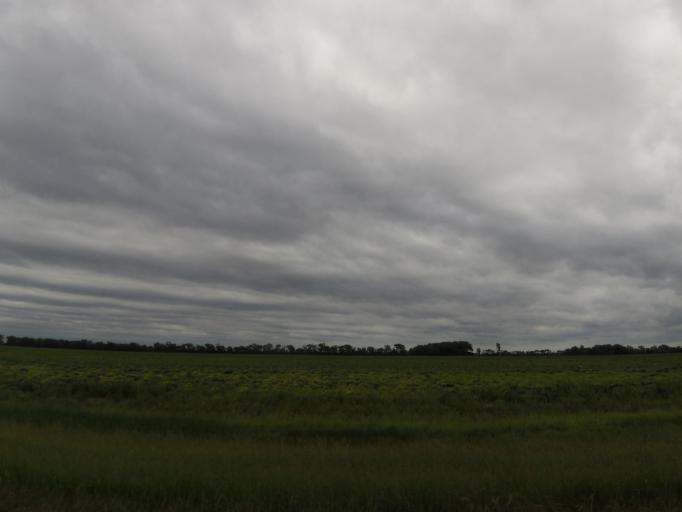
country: US
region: North Dakota
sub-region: Walsh County
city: Grafton
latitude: 48.5298
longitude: -97.4476
